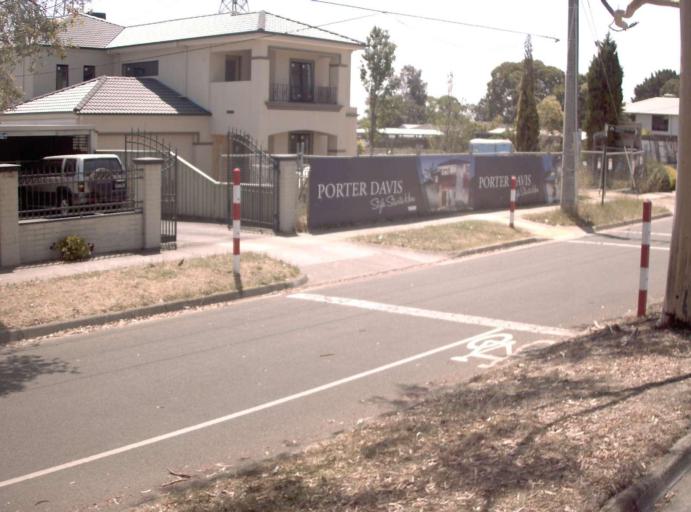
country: AU
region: Victoria
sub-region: Monash
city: Notting Hill
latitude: -37.8961
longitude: 145.1629
